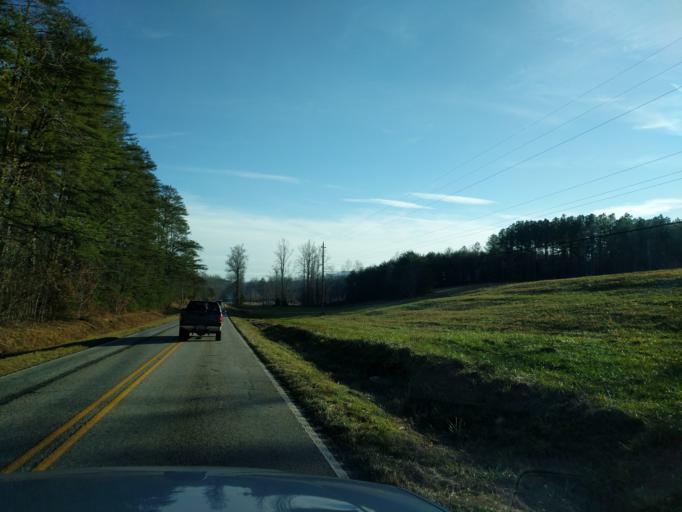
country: US
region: North Carolina
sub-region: Rutherford County
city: Lake Lure
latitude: 35.3936
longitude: -82.1940
